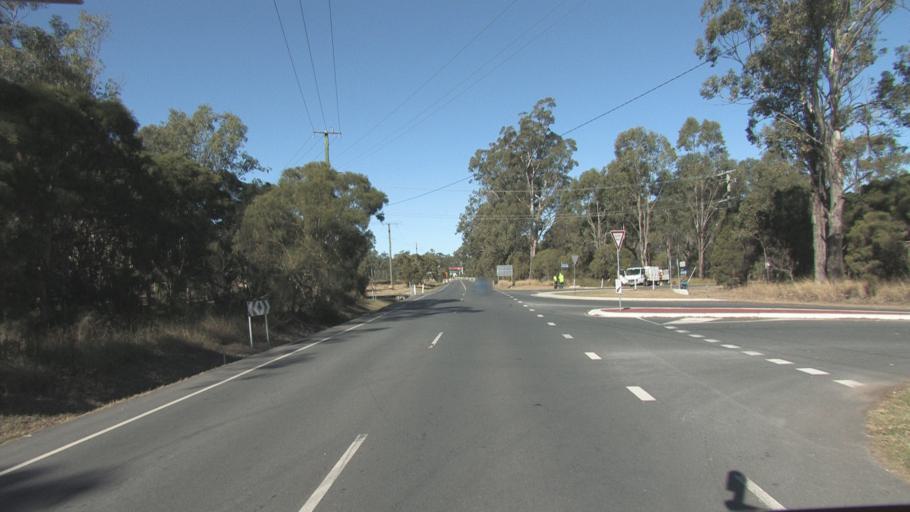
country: AU
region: Queensland
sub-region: Logan
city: North Maclean
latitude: -27.7745
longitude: 153.0084
